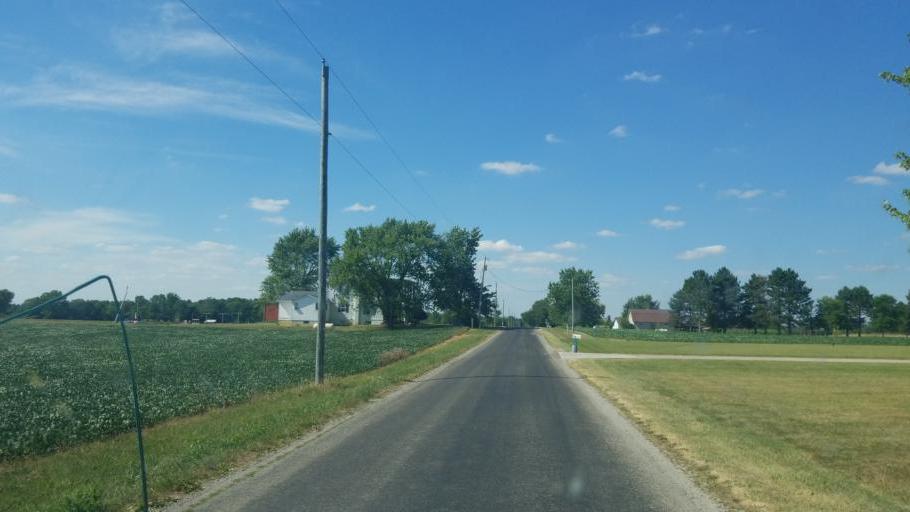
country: US
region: Ohio
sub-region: Defiance County
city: Hicksville
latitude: 41.3653
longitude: -84.7863
